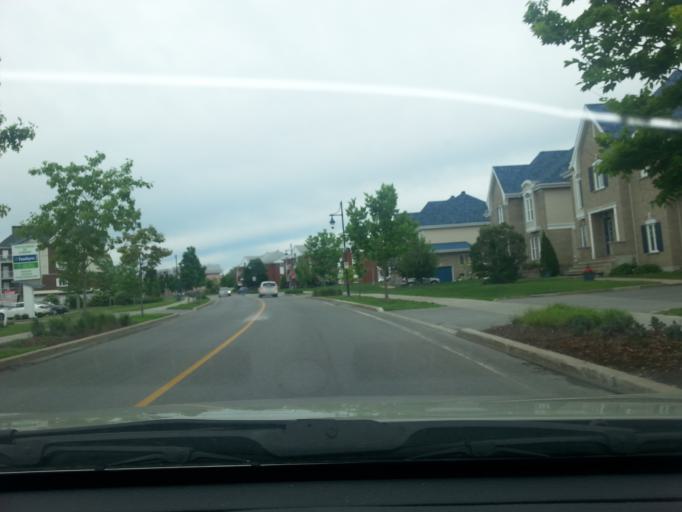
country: CA
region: Quebec
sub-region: Lanaudiere
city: Terrebonne
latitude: 45.6962
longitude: -73.6141
